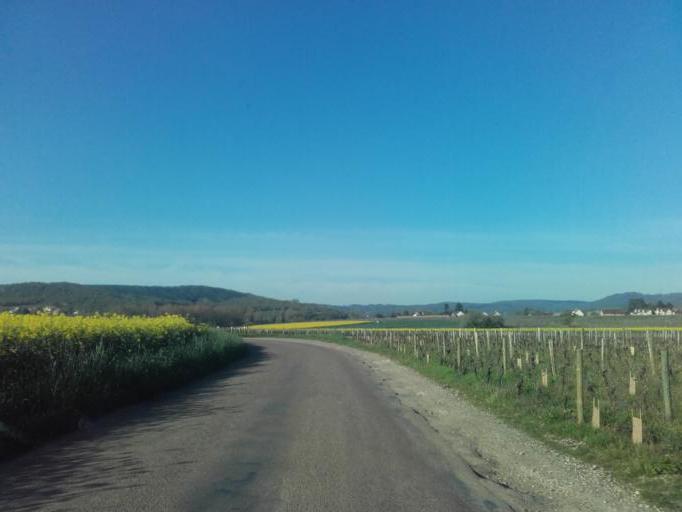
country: FR
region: Bourgogne
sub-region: Departement de Saone-et-Loire
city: Mellecey
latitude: 46.8185
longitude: 4.7262
